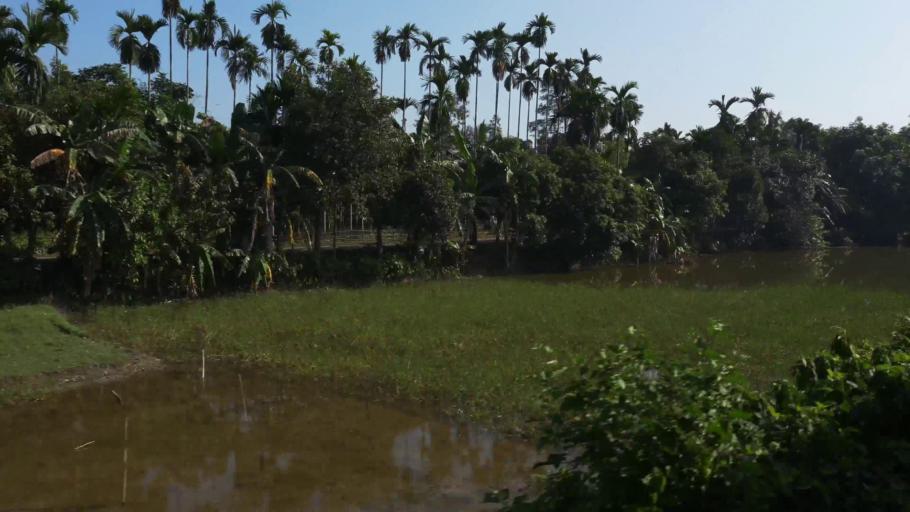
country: BD
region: Dhaka
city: Mymensingh
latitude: 24.7862
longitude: 90.3392
